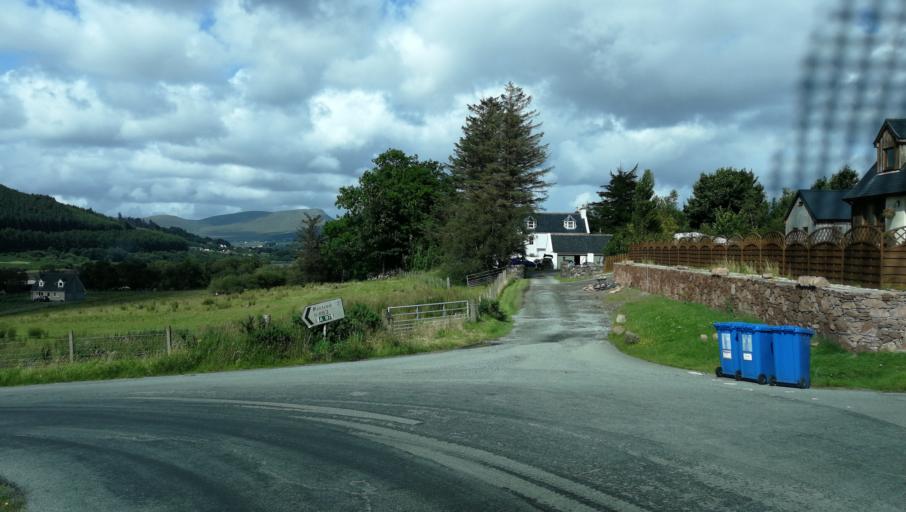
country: GB
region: Scotland
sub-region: Highland
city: Portree
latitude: 57.3871
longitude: -6.1951
